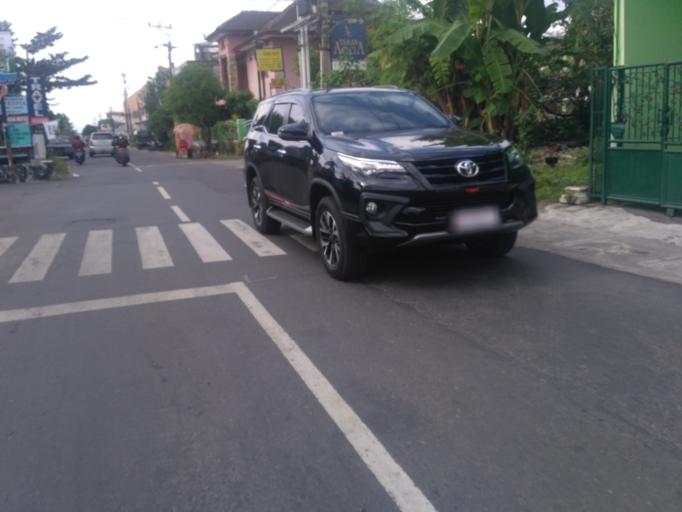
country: ID
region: Daerah Istimewa Yogyakarta
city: Yogyakarta
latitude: -7.7686
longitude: 110.3555
